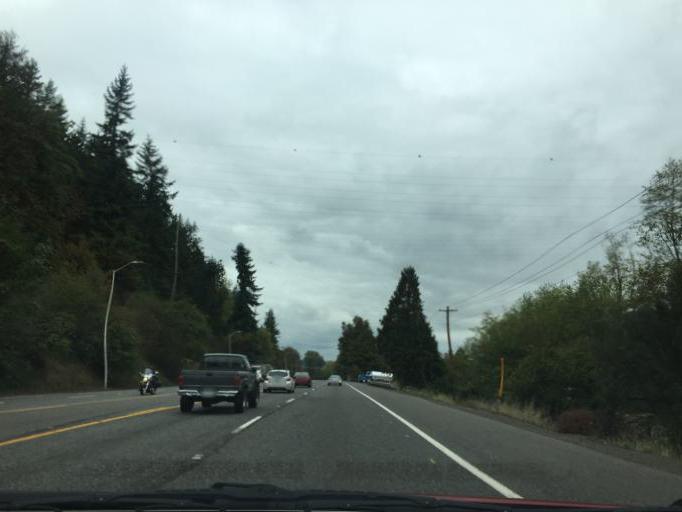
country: US
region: Oregon
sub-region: Washington County
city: Oak Hills
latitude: 45.6093
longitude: -122.7946
